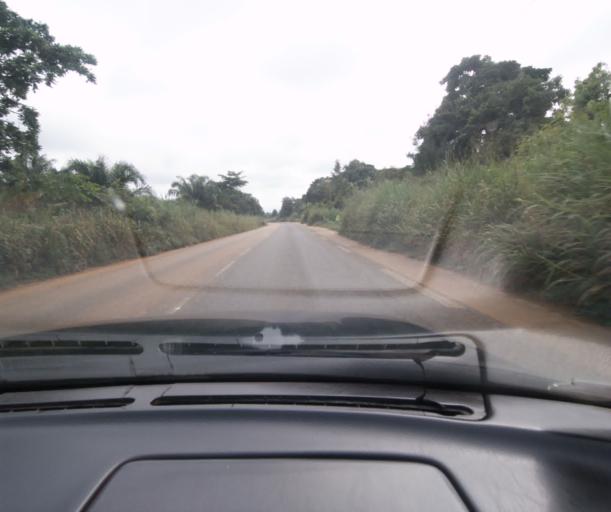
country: CM
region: Centre
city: Ombesa
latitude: 4.4131
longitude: 11.2484
